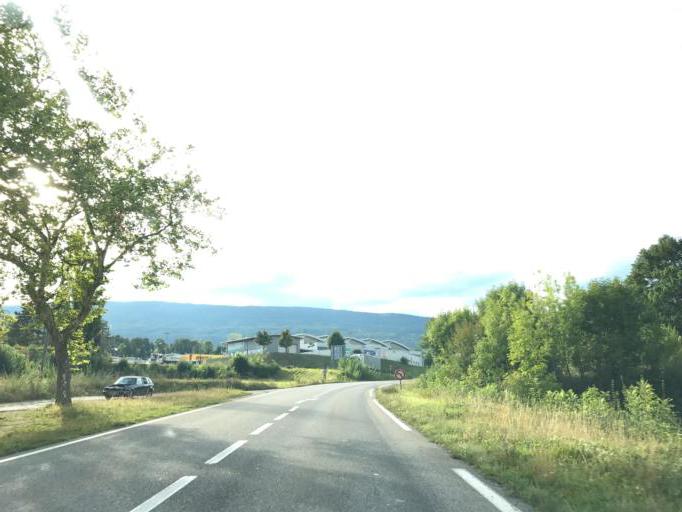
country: FR
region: Rhone-Alpes
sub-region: Departement de l'Ain
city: Lancrans
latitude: 46.1258
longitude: 5.8166
